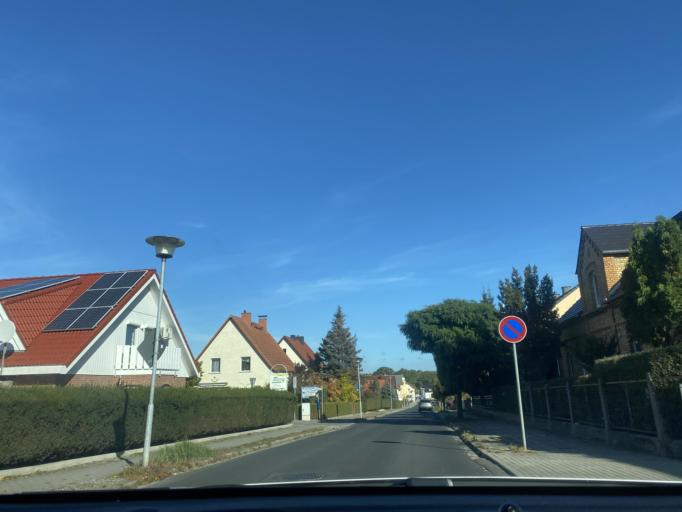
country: DE
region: Saxony
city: Weisswasser
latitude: 51.5038
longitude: 14.6259
